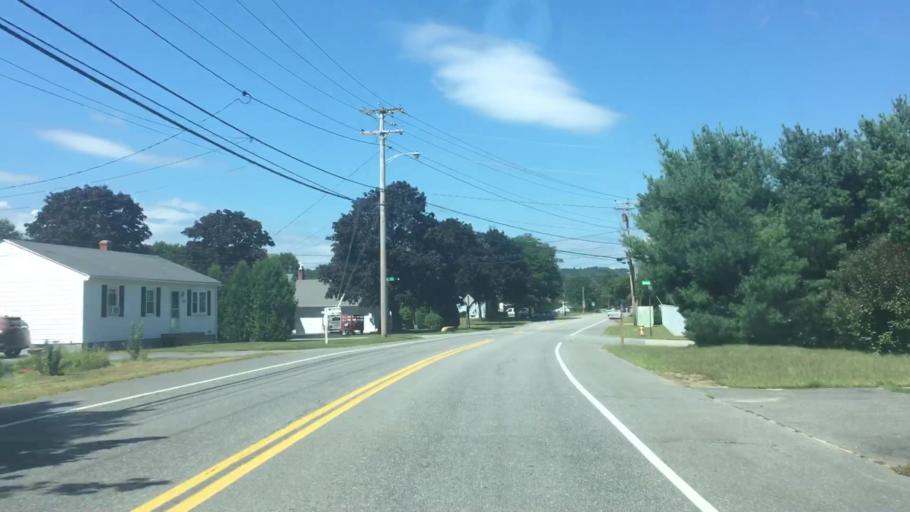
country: US
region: Maine
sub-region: Androscoggin County
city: Sabattus
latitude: 44.0953
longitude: -70.1548
